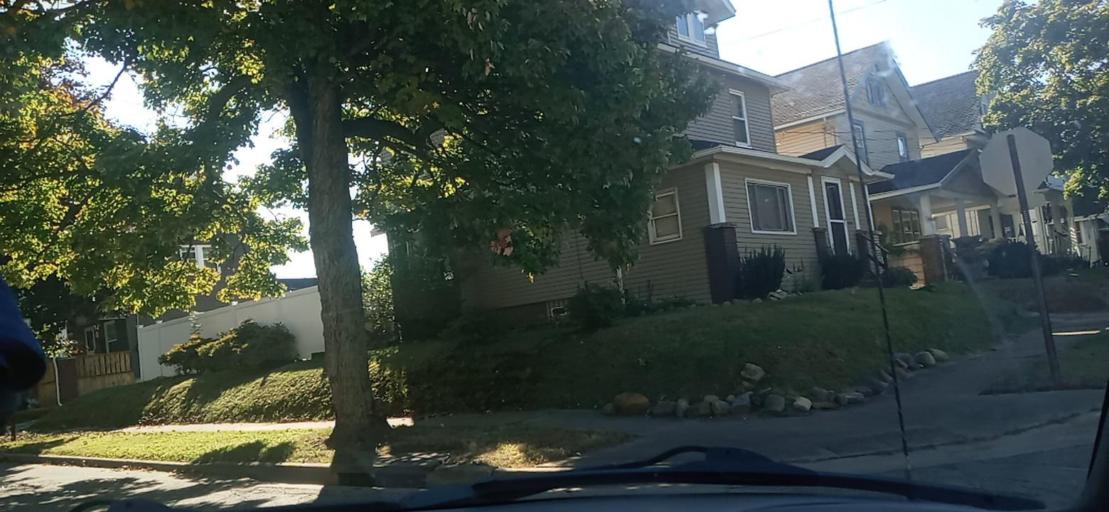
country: US
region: Ohio
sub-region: Summit County
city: Barberton
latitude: 41.0417
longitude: -81.5704
